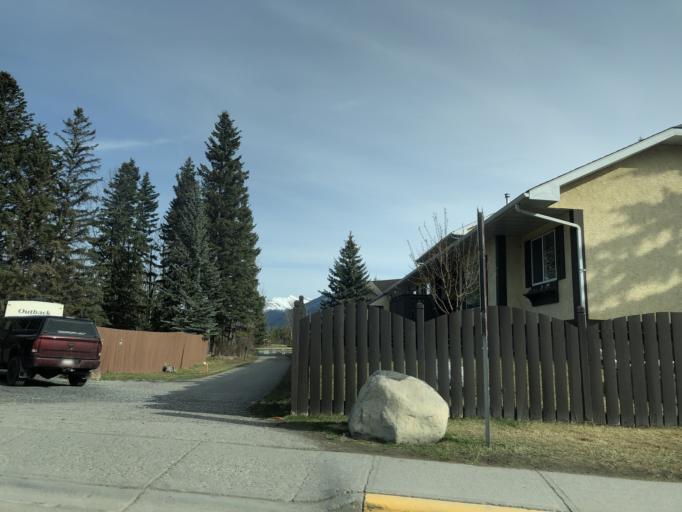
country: CA
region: Alberta
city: Canmore
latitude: 51.0827
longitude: -115.3672
